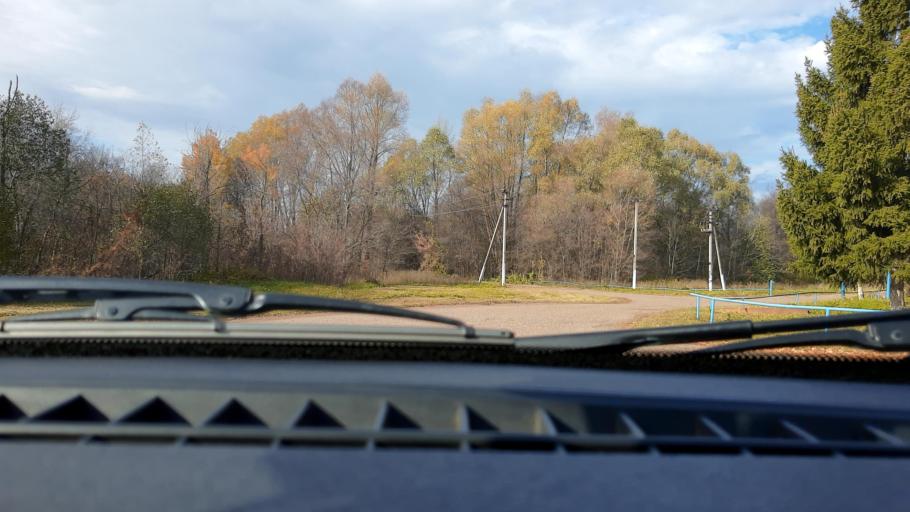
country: RU
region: Bashkortostan
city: Mikhaylovka
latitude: 54.8054
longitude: 55.8312
